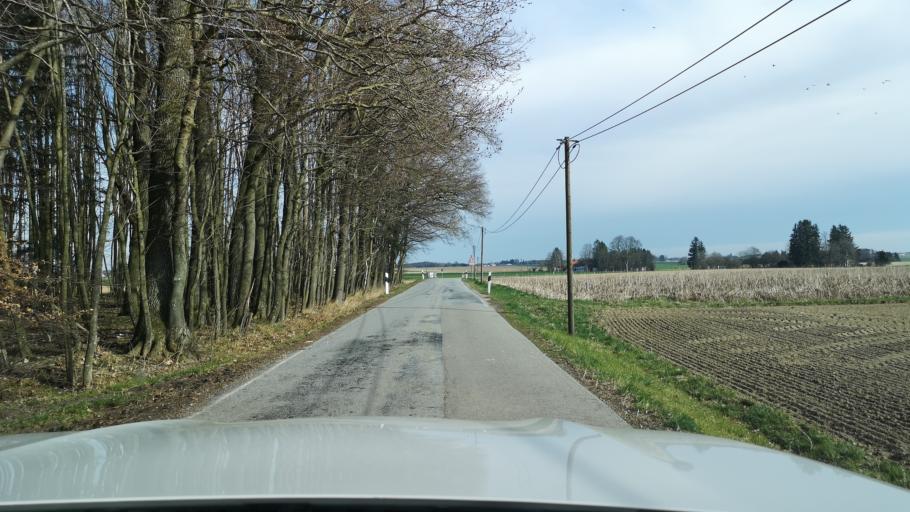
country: DE
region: Bavaria
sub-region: Upper Bavaria
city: Buch am Buchrain
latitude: 48.2145
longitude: 11.9703
